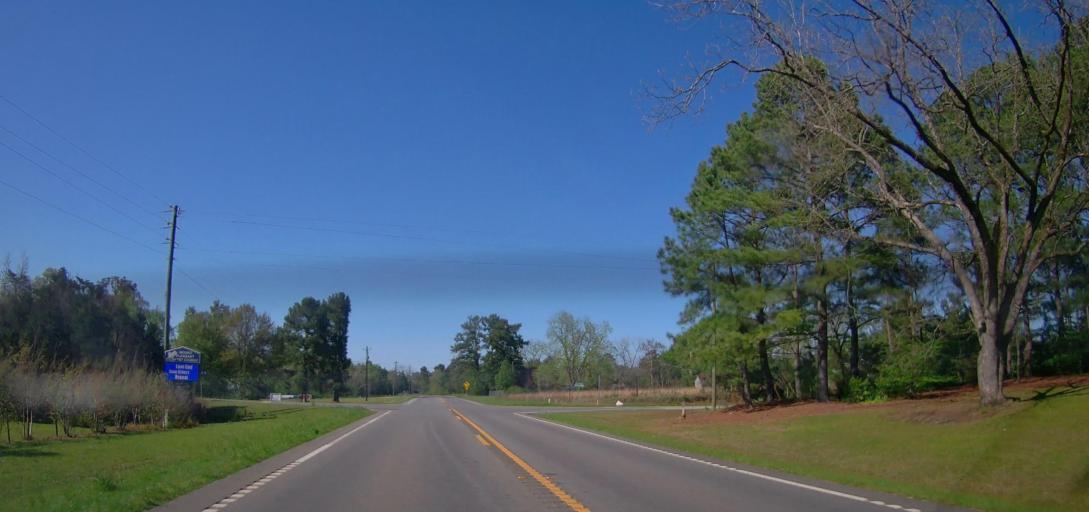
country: US
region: Georgia
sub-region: Pulaski County
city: Hawkinsville
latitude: 32.1257
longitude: -83.5006
